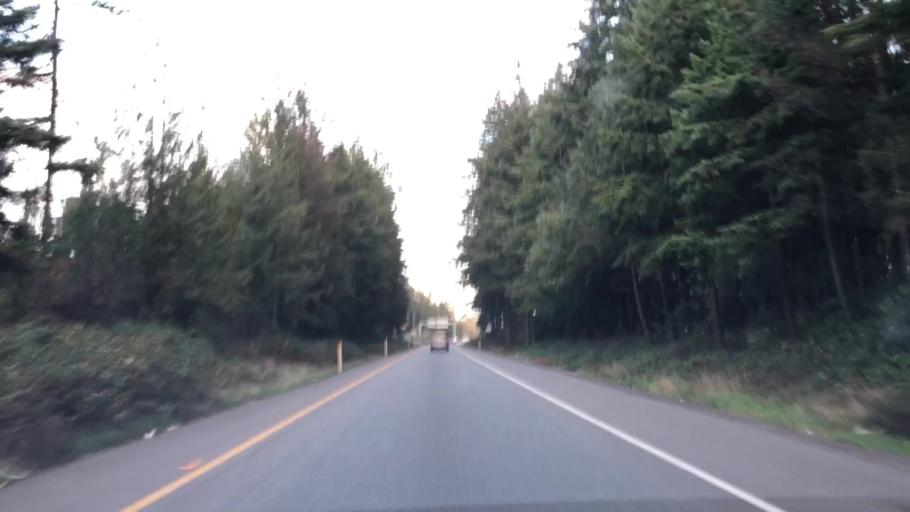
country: US
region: Washington
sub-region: King County
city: Lakeland South
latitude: 47.2878
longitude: -122.3053
